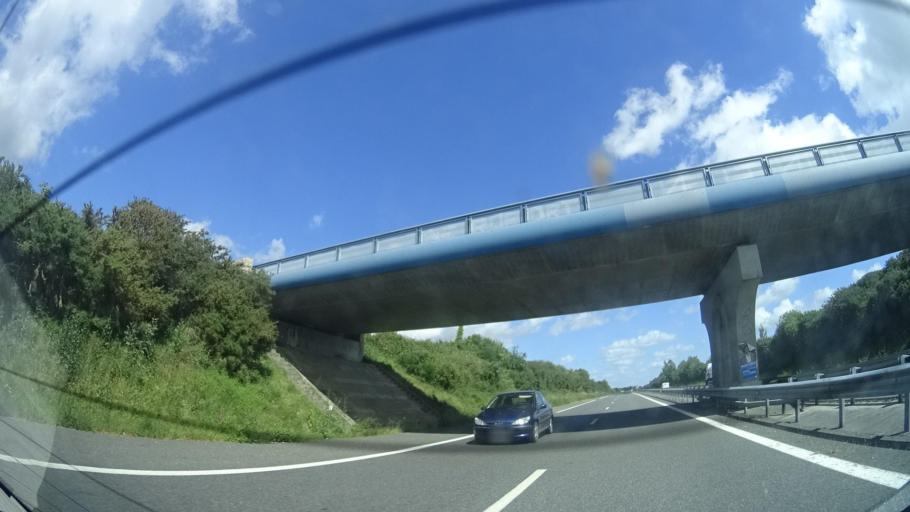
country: FR
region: Brittany
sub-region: Departement du Morbihan
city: Limerzel
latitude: 47.6697
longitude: -2.3343
